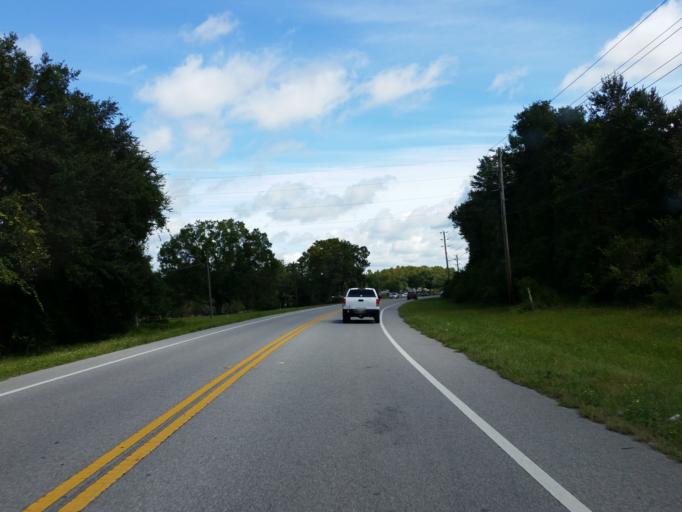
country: US
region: Florida
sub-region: Pasco County
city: Wesley Chapel
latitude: 28.2201
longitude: -82.3861
